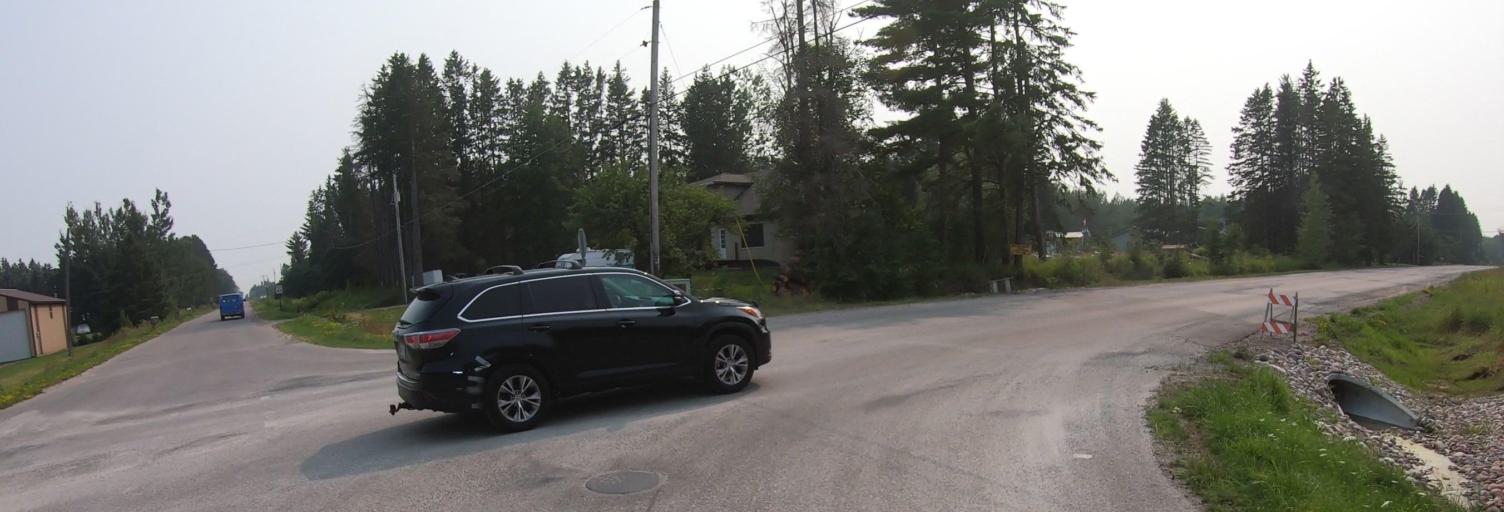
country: US
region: Michigan
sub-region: Chippewa County
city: Sault Ste. Marie
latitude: 46.4628
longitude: -84.3013
